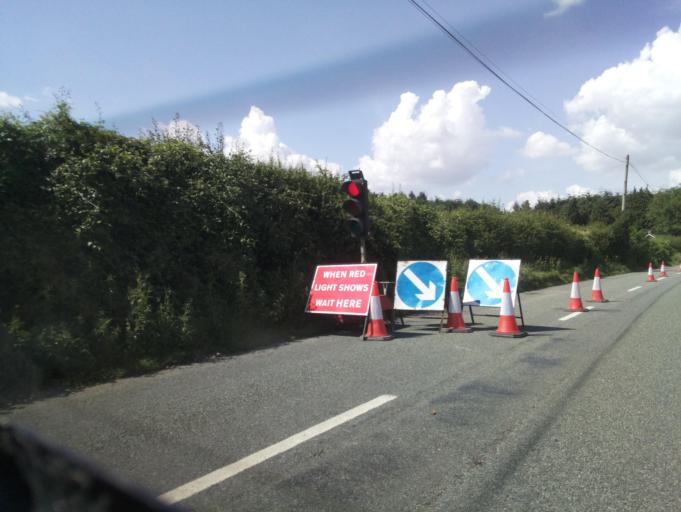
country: GB
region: England
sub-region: West Berkshire
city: Farnborough
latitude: 51.4880
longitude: -1.3646
